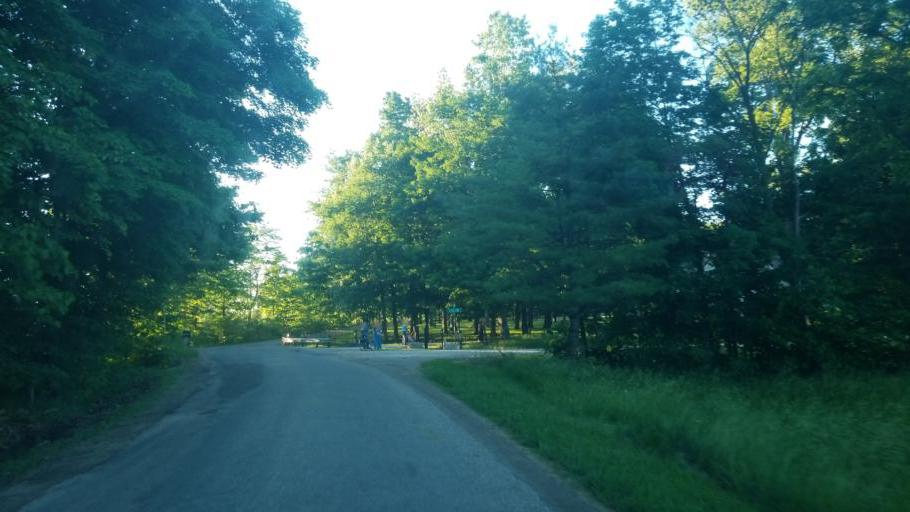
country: US
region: Indiana
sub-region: Elkhart County
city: Nappanee
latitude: 41.4351
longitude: -86.0493
